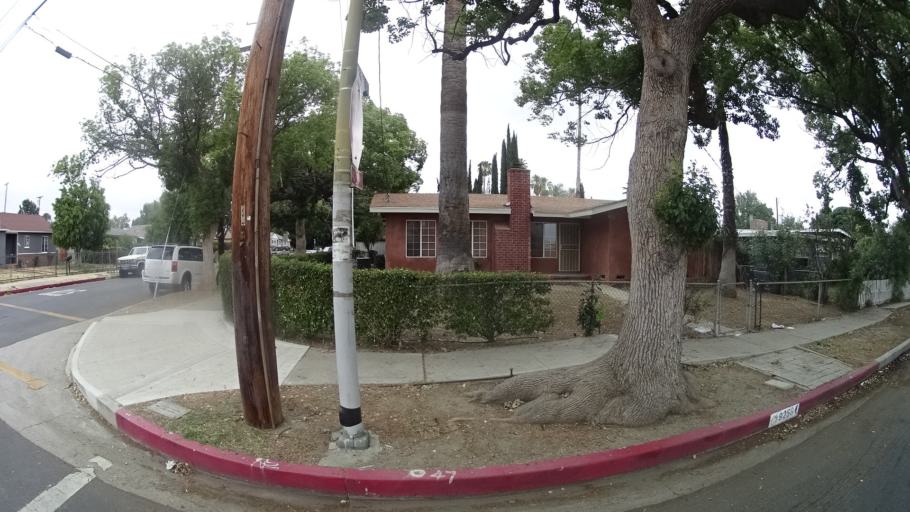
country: US
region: California
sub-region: Los Angeles County
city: San Fernando
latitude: 34.2390
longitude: -118.4588
